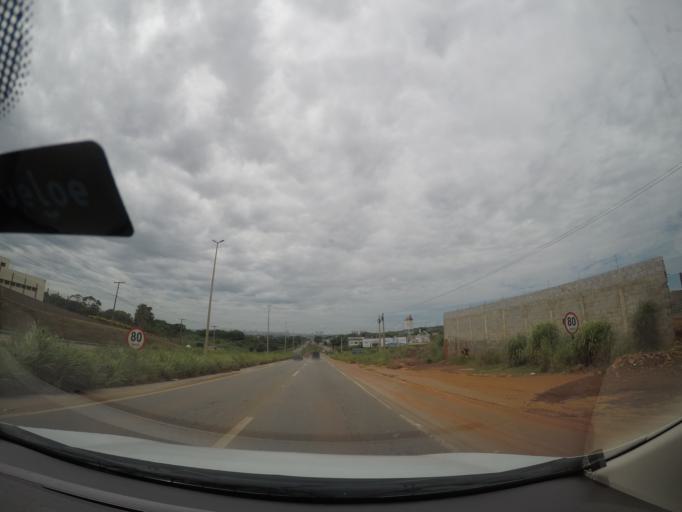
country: BR
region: Goias
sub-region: Goiania
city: Goiania
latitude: -16.6316
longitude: -49.3487
